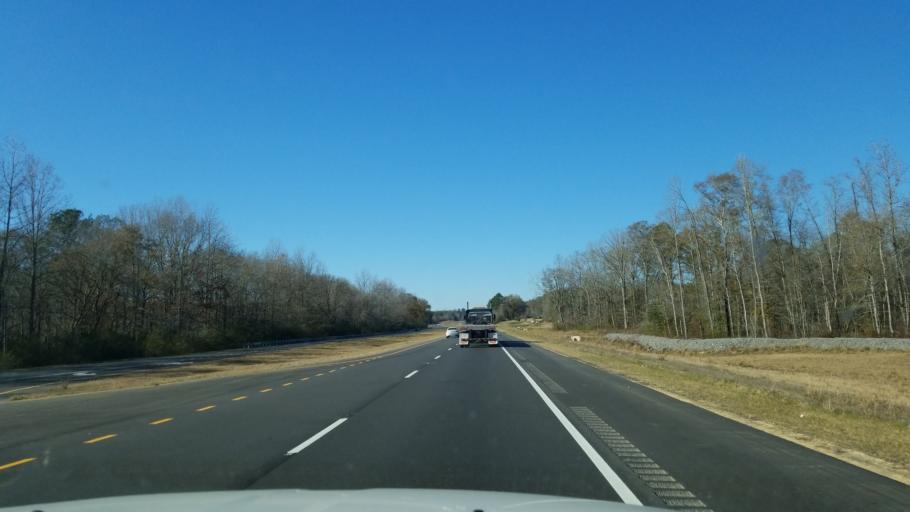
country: US
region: Alabama
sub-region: Pickens County
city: Gordo
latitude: 33.3470
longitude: -87.9506
